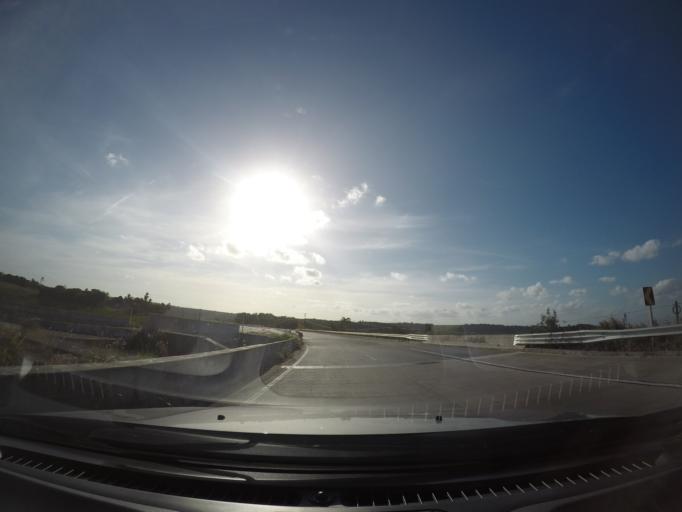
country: BR
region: Alagoas
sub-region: Pilar
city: Pilar
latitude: -9.5858
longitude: -35.9996
